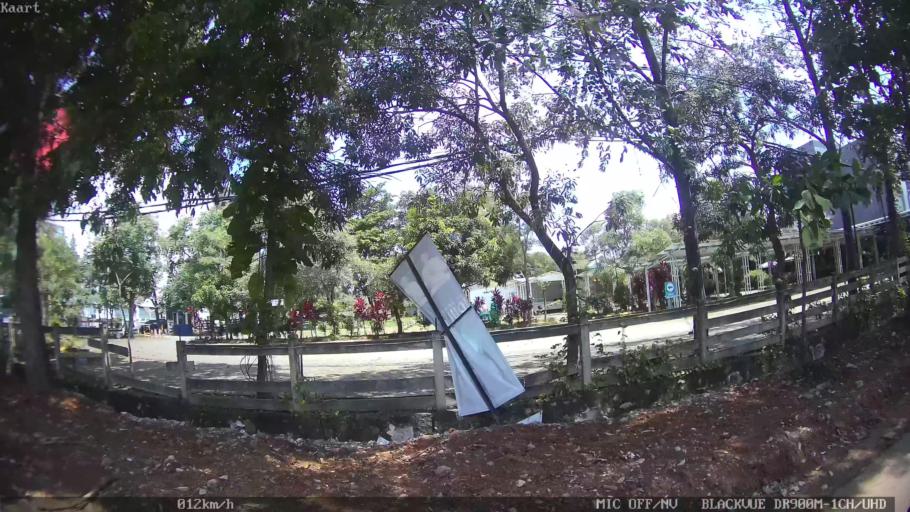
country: ID
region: Lampung
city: Kedaton
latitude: -5.3829
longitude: 105.2813
